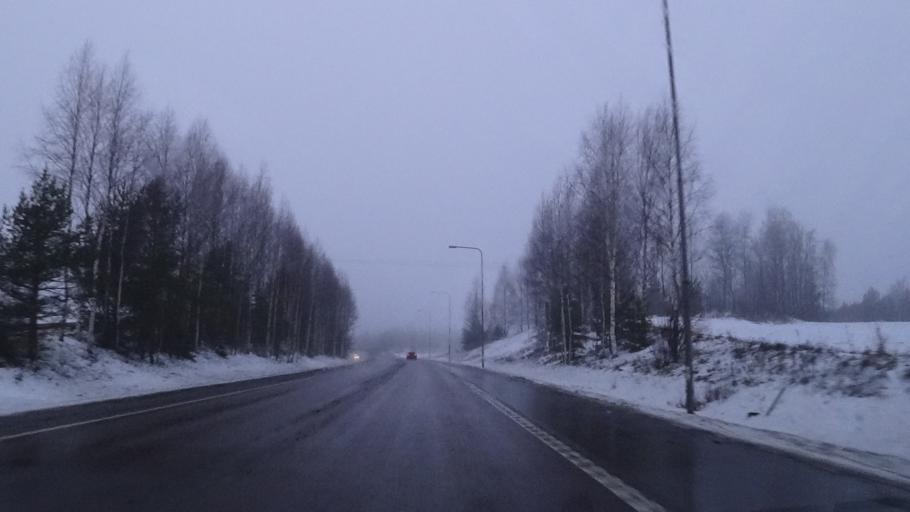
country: FI
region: Paijanne Tavastia
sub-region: Lahti
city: Hollola
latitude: 60.9829
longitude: 25.4571
